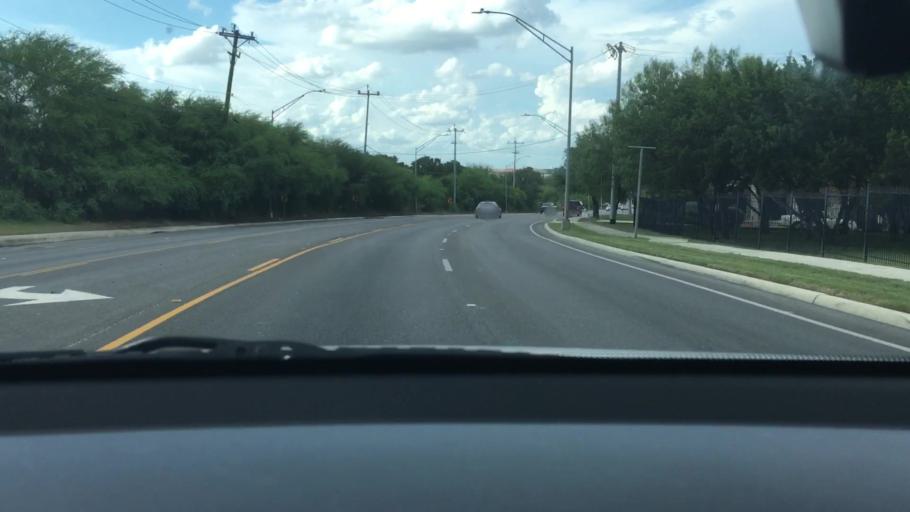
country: US
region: Texas
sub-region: Bexar County
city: Live Oak
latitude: 29.5988
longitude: -98.4045
